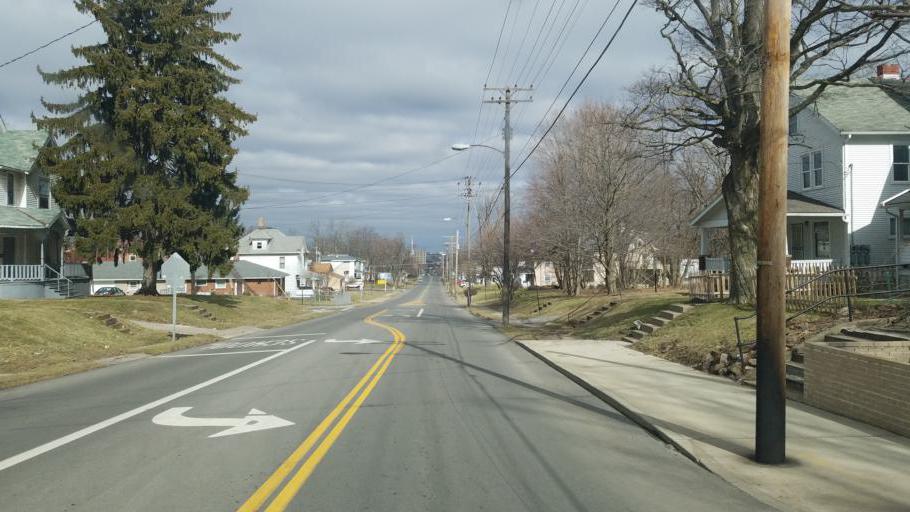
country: US
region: Ohio
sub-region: Richland County
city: Mansfield
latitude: 40.7477
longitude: -82.5164
